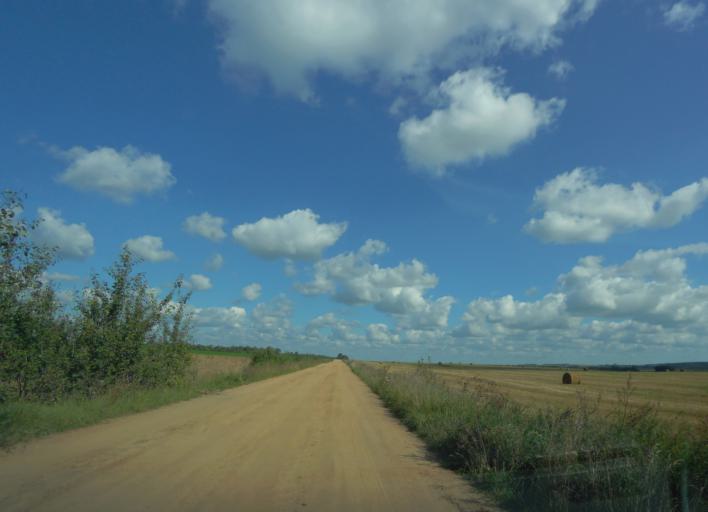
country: BY
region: Minsk
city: Zyembin
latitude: 54.3702
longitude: 28.3439
